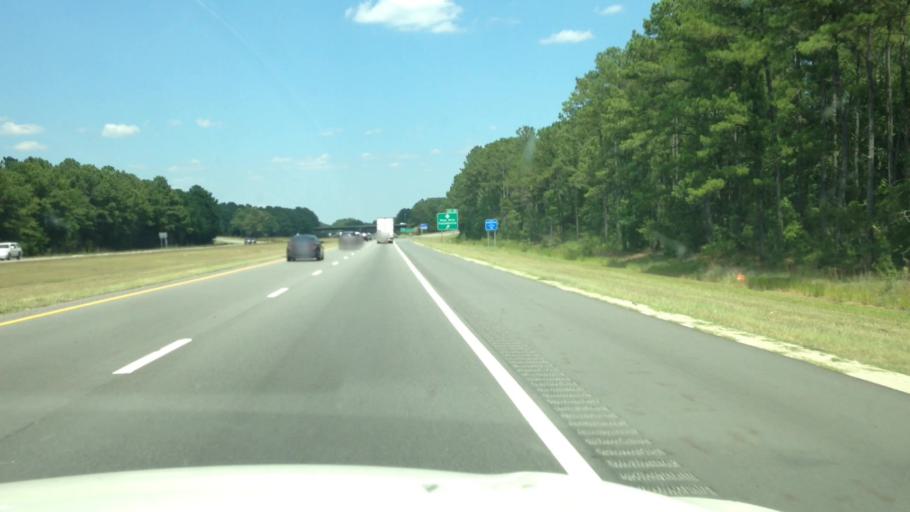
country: US
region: North Carolina
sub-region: Cumberland County
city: Hope Mills
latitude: 34.9354
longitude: -78.9293
